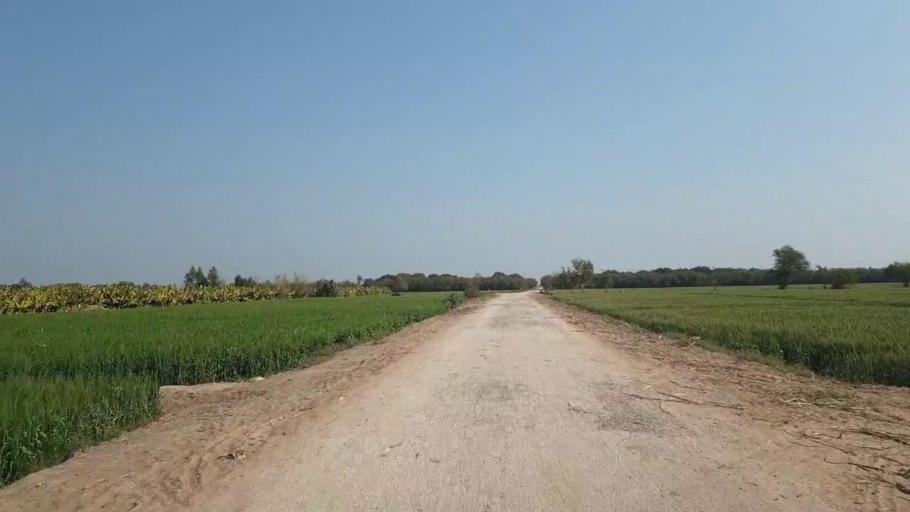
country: PK
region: Sindh
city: Hala
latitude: 25.9497
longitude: 68.4708
